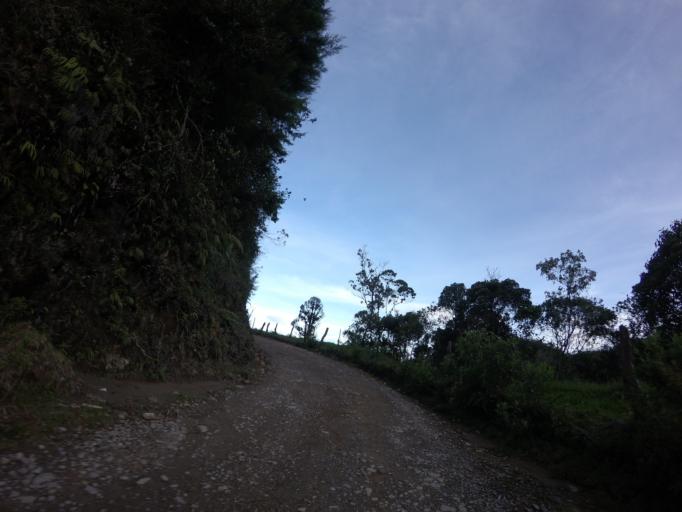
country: CO
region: Caldas
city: Pensilvania
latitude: 5.4405
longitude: -75.1302
